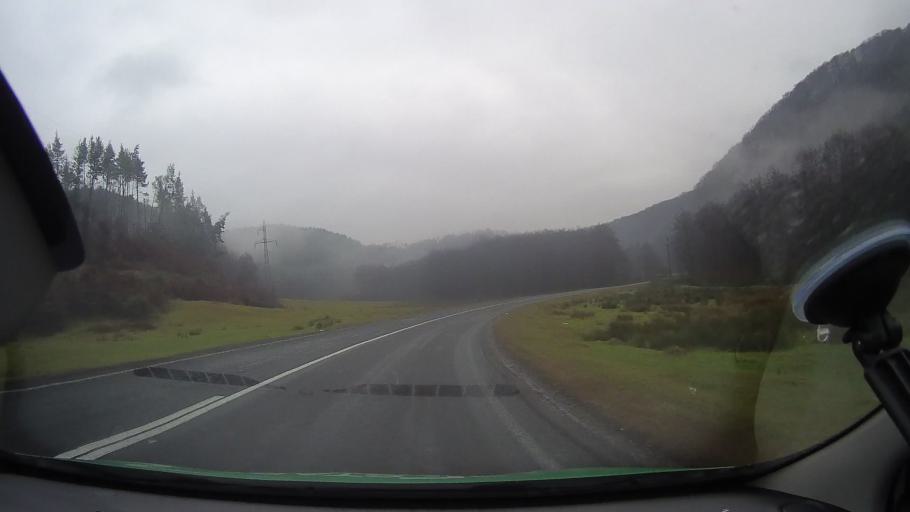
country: RO
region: Arad
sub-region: Comuna Plescuta
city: Plescuta
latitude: 46.3180
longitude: 22.4609
